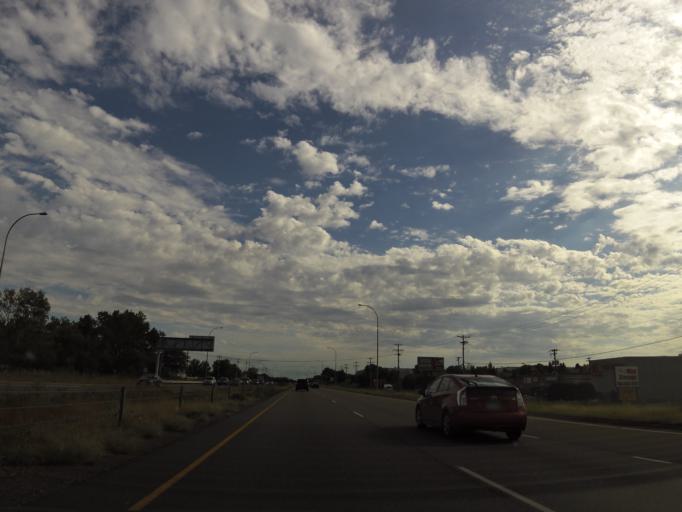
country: US
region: Minnesota
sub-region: Hennepin County
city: New Hope
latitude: 45.0543
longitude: -93.4010
